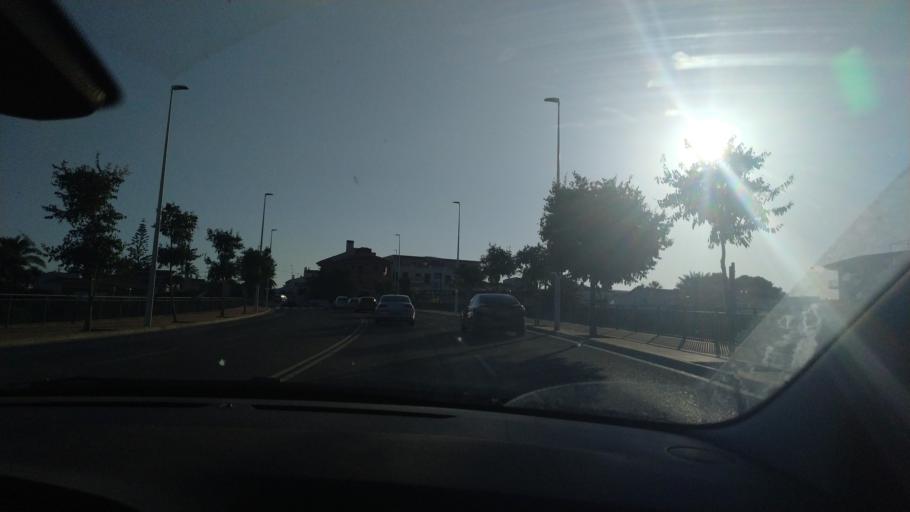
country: ES
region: Valencia
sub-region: Provincia de Alicante
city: Javea
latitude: 38.7855
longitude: 0.1614
